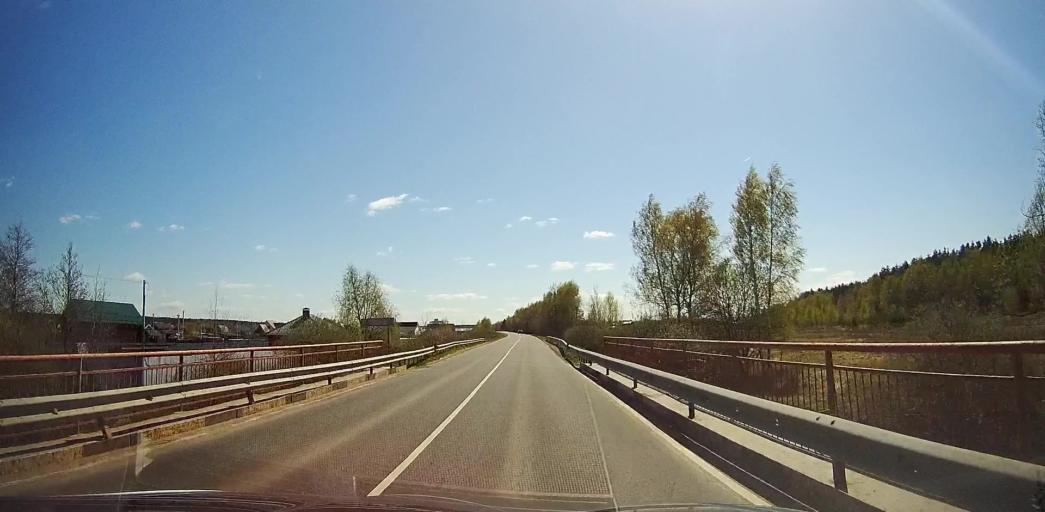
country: RU
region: Moskovskaya
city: Beloozerskiy
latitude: 55.5294
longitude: 38.4300
